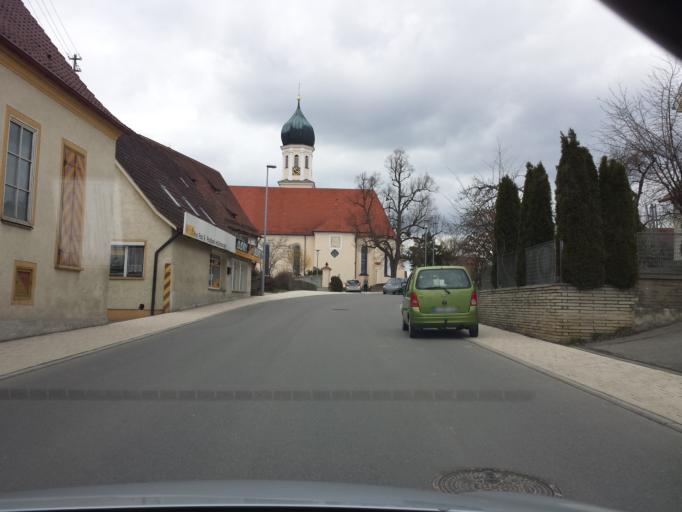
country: DE
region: Baden-Wuerttemberg
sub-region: Tuebingen Region
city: Schwendi
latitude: 48.1781
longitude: 9.9752
